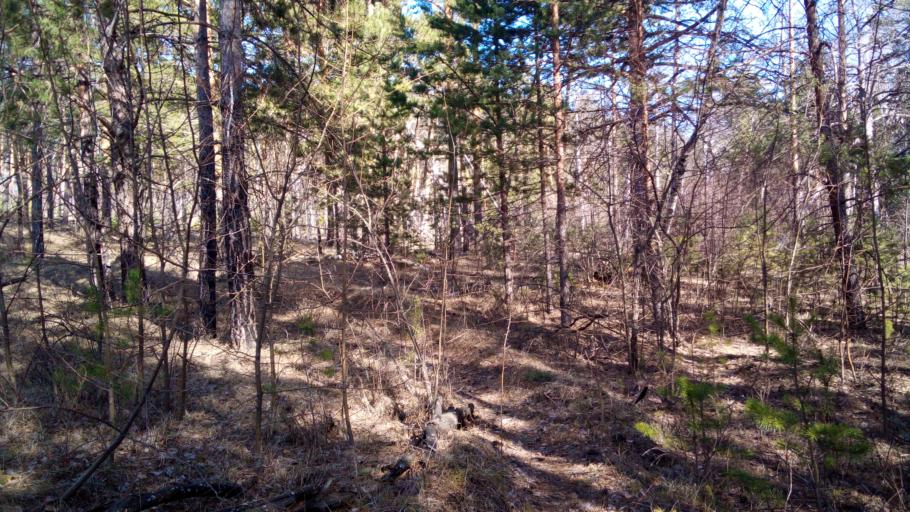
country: RU
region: Chelyabinsk
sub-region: Gorod Chelyabinsk
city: Chelyabinsk
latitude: 55.1587
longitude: 61.3280
